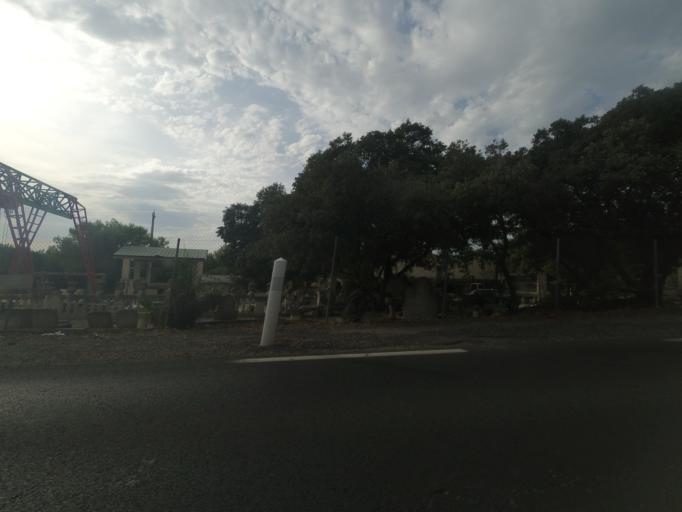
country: FR
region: Languedoc-Roussillon
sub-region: Departement de l'Herault
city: Saint-Genies-des-Mourgues
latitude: 43.7002
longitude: 4.0190
